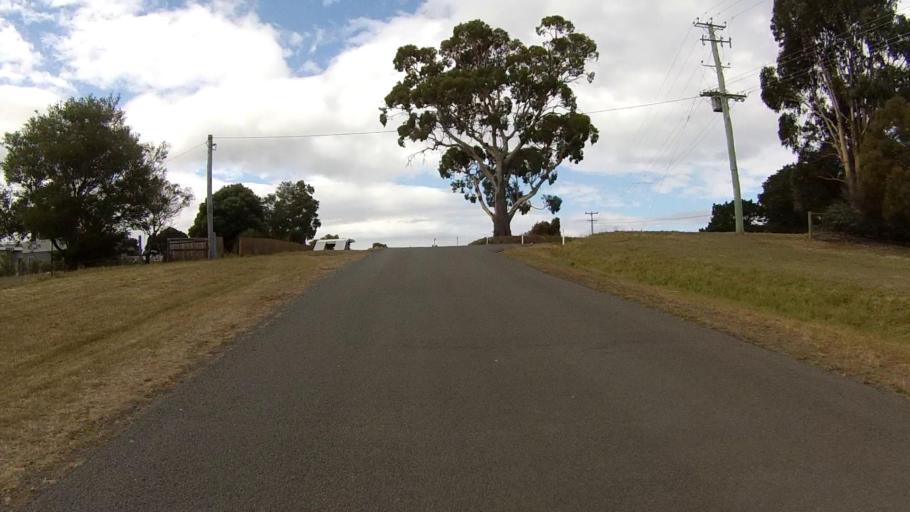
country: AU
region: Tasmania
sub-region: Clarence
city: Seven Mile Beach
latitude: -42.8566
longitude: 147.4831
